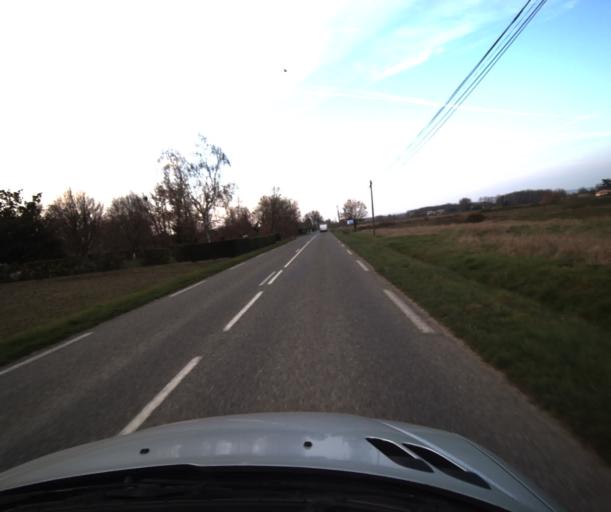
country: FR
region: Midi-Pyrenees
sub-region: Departement de la Haute-Garonne
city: Fronton
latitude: 43.8627
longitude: 1.3828
